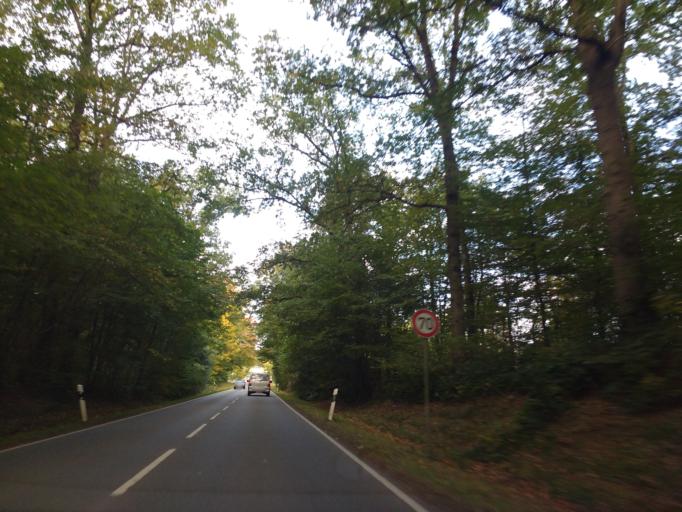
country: DE
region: Schleswig-Holstein
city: Schonwalde am Bungsberg
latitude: 54.1819
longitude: 10.7683
